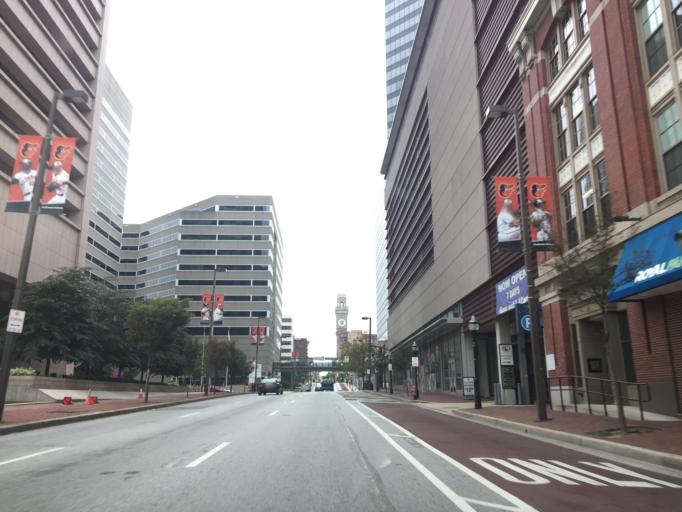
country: US
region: Maryland
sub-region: City of Baltimore
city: Baltimore
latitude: 39.2878
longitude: -76.6139
